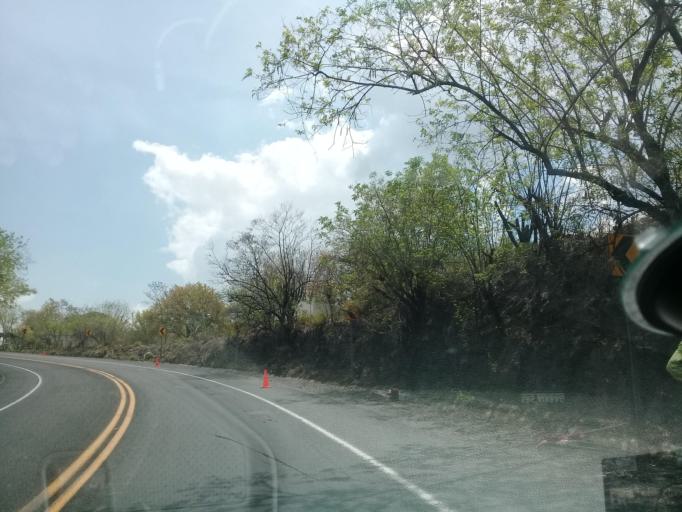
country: MX
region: Veracruz
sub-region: Emiliano Zapata
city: Plan del Rio
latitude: 19.4029
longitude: -96.6466
